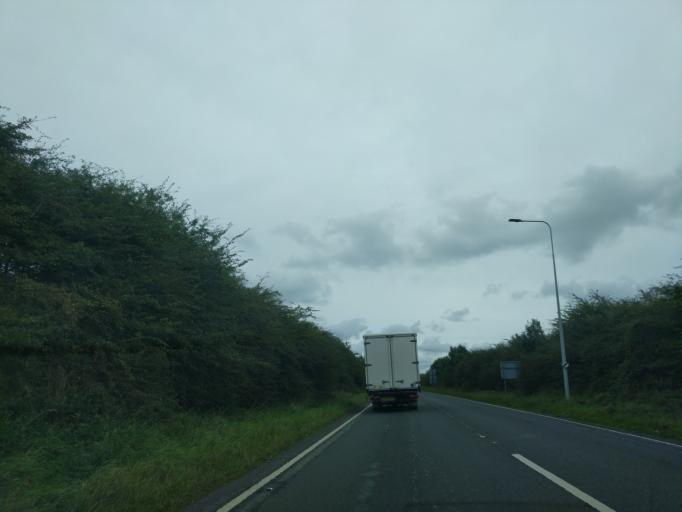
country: GB
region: England
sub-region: Cheshire East
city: Weston
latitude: 53.0587
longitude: -2.3990
